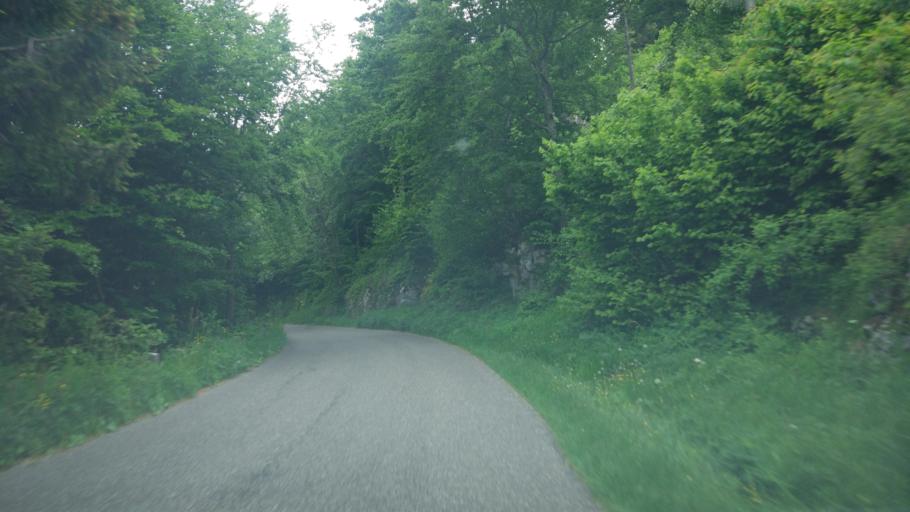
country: IT
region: Veneto
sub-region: Provincia di Verona
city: Erbezzo
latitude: 45.6582
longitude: 11.0039
